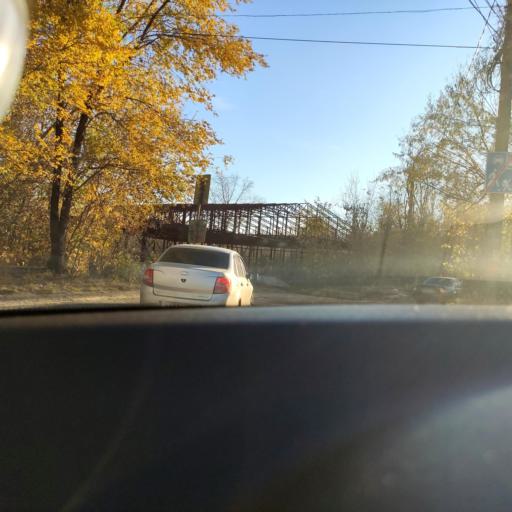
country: RU
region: Samara
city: Smyshlyayevka
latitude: 53.1902
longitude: 50.2789
